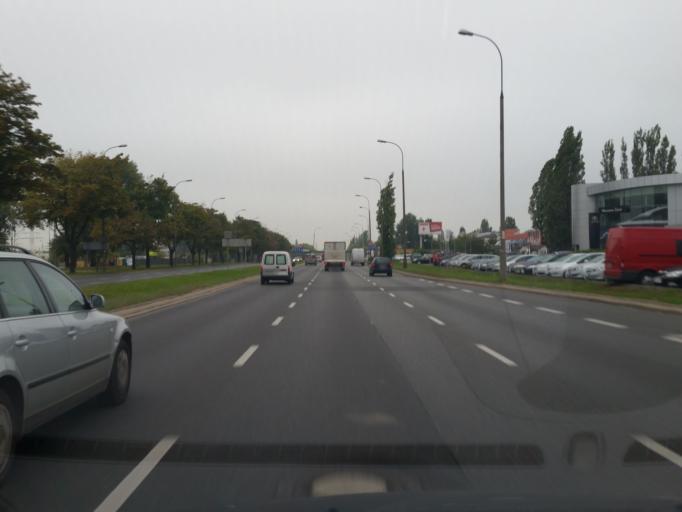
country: PL
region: Masovian Voivodeship
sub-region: Warszawa
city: Zoliborz
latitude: 52.2749
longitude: 21.0143
